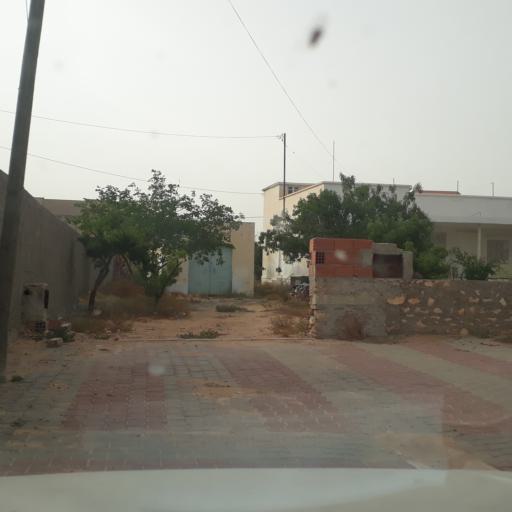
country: TN
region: Safaqis
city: Al Qarmadah
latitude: 34.8142
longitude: 10.7679
